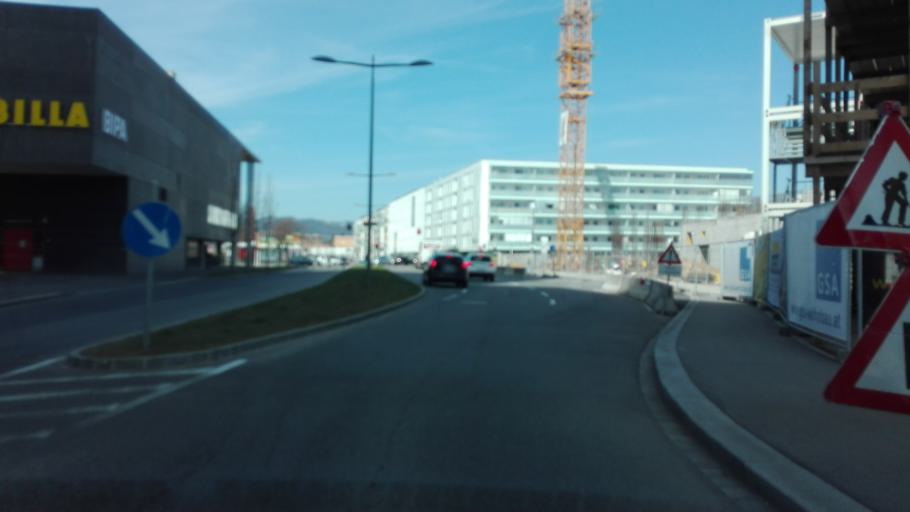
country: AT
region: Upper Austria
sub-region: Linz Stadt
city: Linz
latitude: 48.2914
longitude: 14.3054
